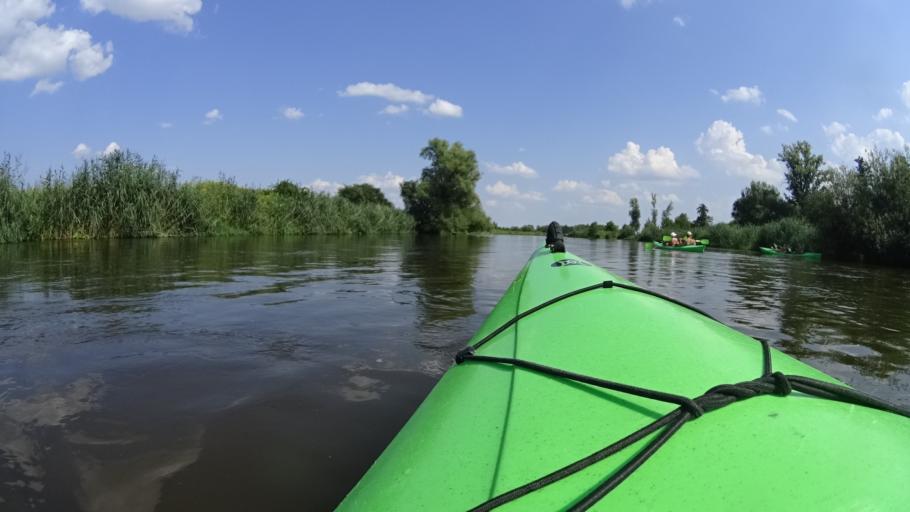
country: PL
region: Masovian Voivodeship
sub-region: Powiat bialobrzeski
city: Wysmierzyce
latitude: 51.6575
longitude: 20.8364
